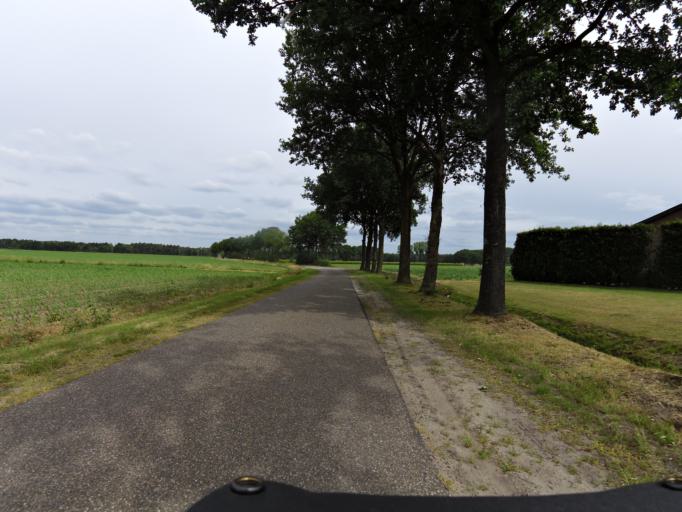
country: BE
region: Flanders
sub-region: Provincie Antwerpen
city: Arendonk
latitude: 51.3895
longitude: 5.1137
